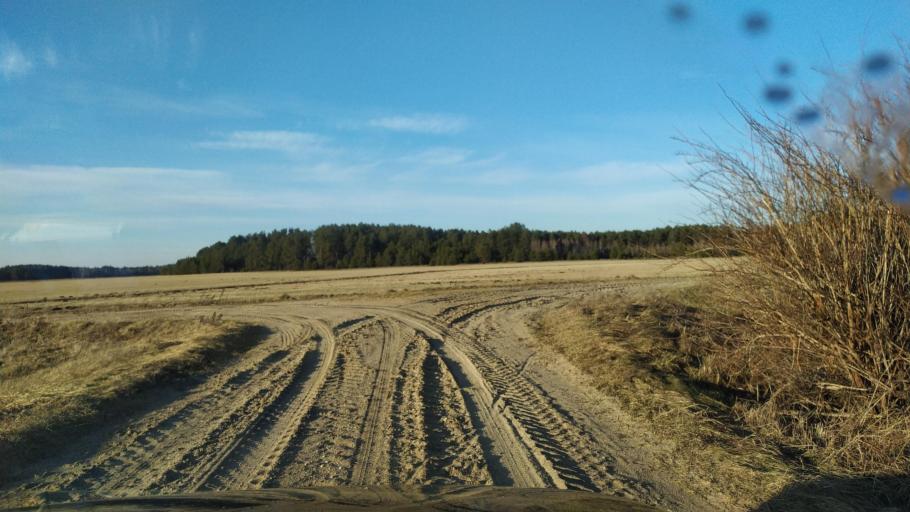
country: BY
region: Brest
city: Pruzhany
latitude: 52.5528
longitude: 24.3027
